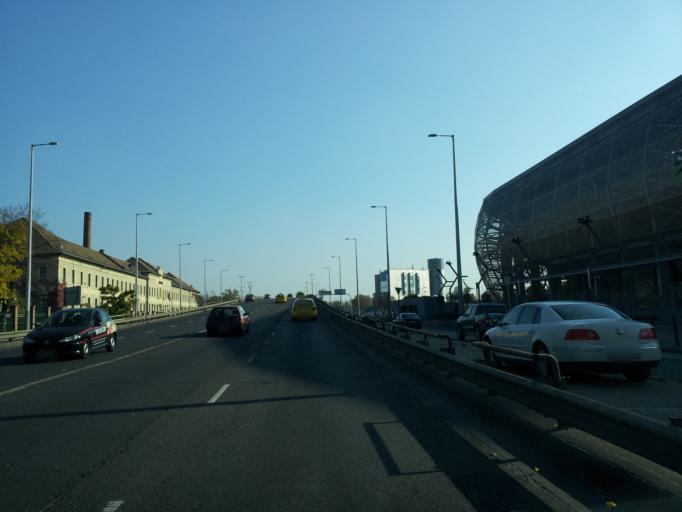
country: HU
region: Budapest
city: Budapest VIII. keruelet
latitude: 47.4768
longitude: 19.0951
